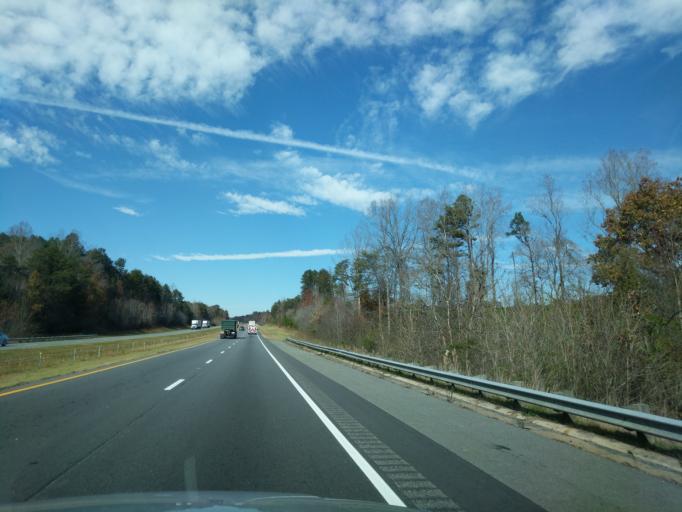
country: US
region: North Carolina
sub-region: Lincoln County
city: Lincolnton
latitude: 35.4312
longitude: -81.2068
